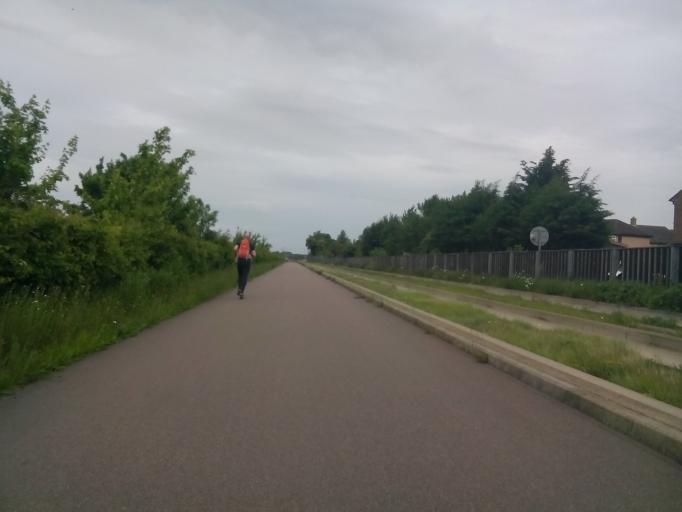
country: GB
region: England
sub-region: Cambridgeshire
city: Histon
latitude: 52.2518
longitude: 0.0951
